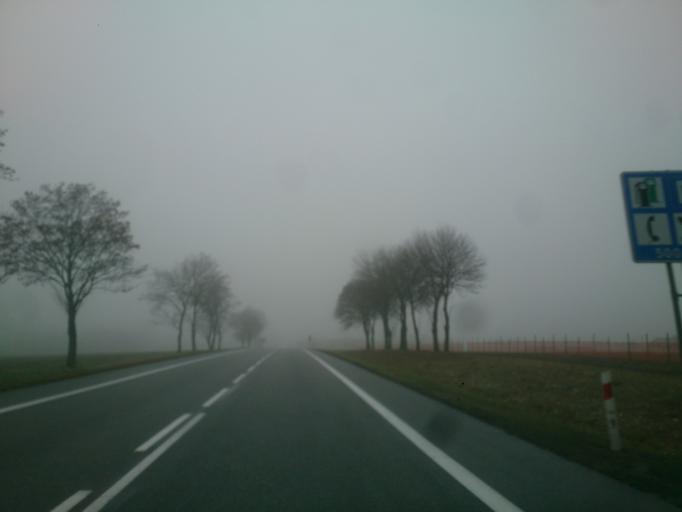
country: PL
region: Masovian Voivodeship
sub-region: Powiat plonski
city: Dzierzaznia
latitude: 52.6371
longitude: 20.1506
